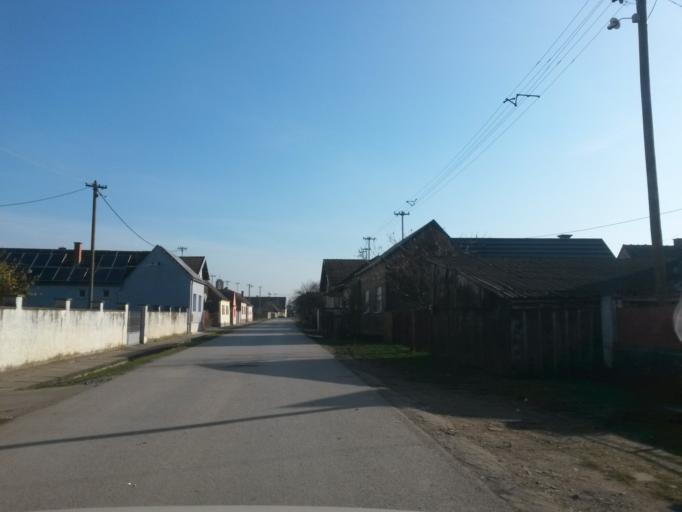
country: HR
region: Vukovarsko-Srijemska
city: Privlaka
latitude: 45.1951
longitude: 18.8349
